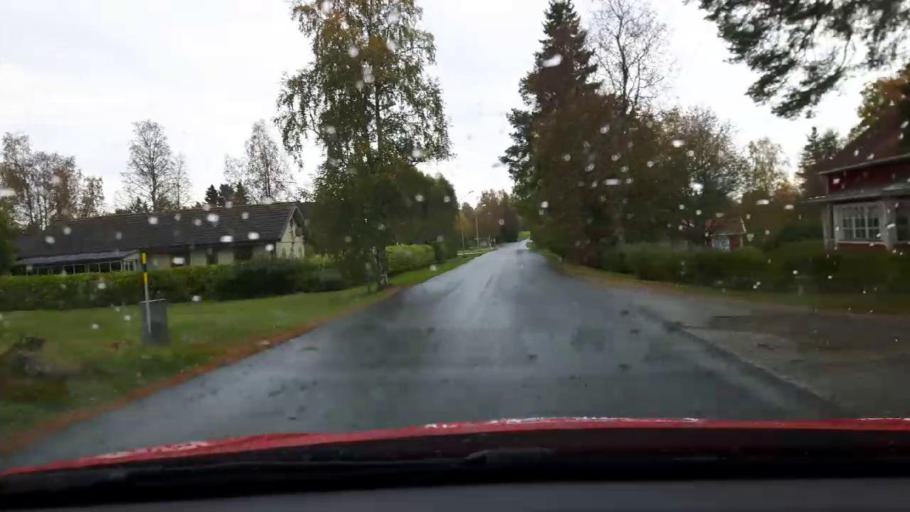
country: SE
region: Jaemtland
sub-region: Bergs Kommun
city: Hoverberg
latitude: 62.9342
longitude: 14.5145
